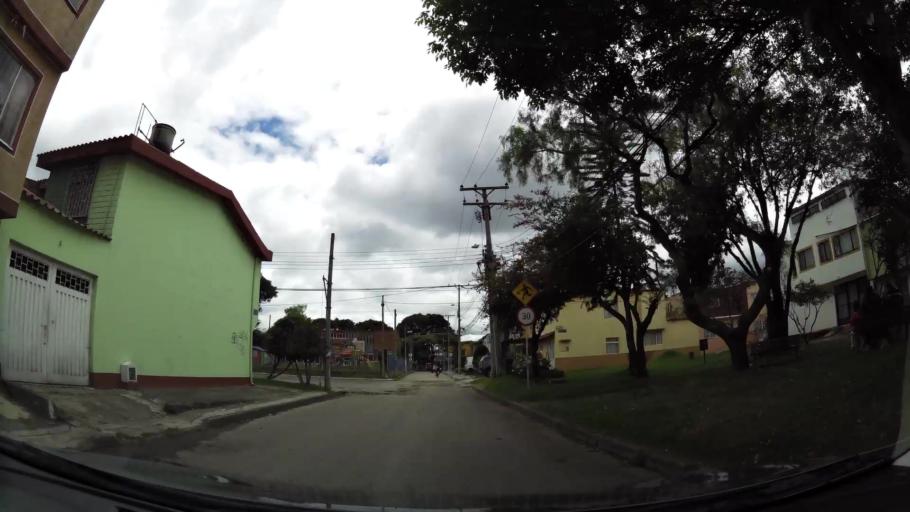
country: CO
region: Bogota D.C.
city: Barrio San Luis
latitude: 4.7032
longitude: -74.0950
